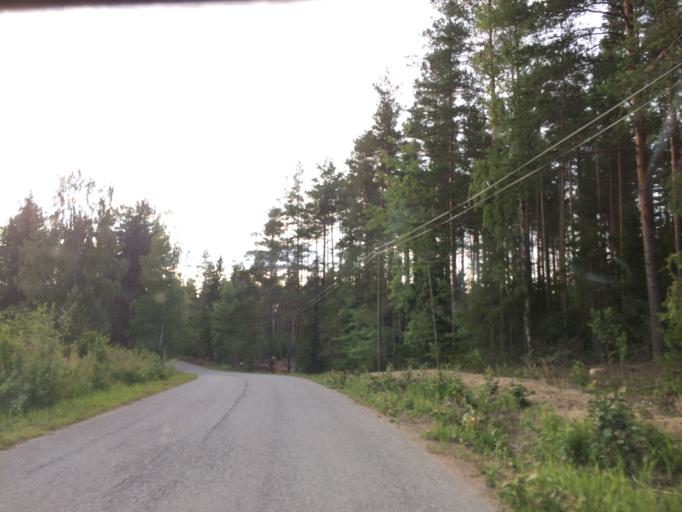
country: FI
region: Haeme
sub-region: Haemeenlinna
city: Tervakoski
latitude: 60.8533
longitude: 24.6192
